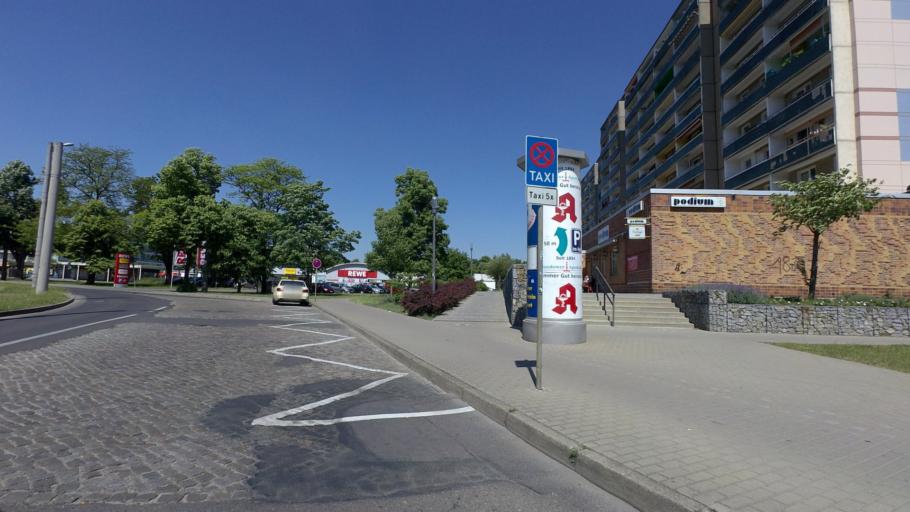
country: DE
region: Brandenburg
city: Cottbus
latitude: 51.7622
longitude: 14.3487
